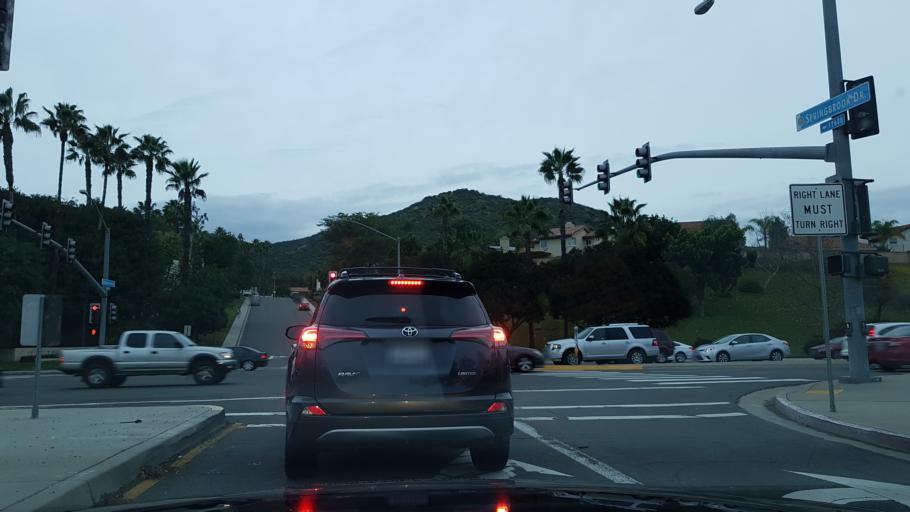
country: US
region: California
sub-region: San Diego County
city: Poway
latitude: 32.9453
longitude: -117.0840
